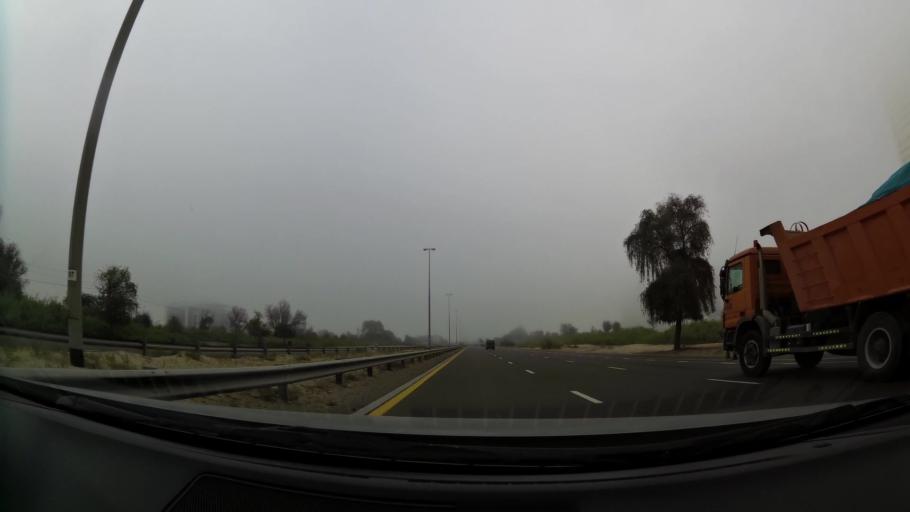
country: AE
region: Dubai
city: Dubai
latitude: 25.0969
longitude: 55.3843
